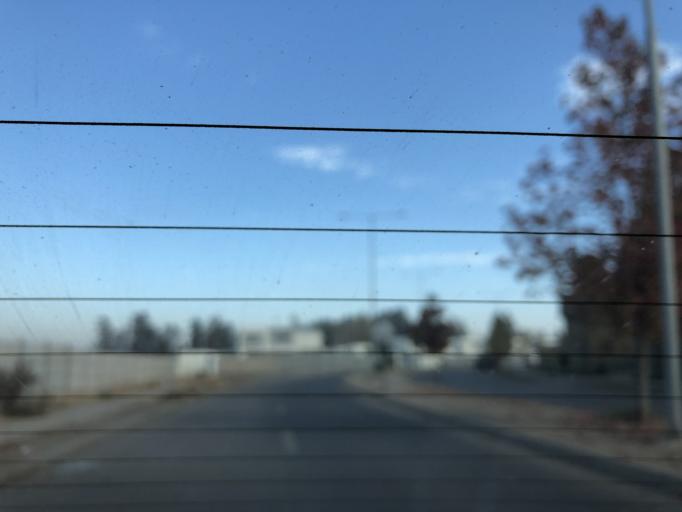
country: CL
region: Santiago Metropolitan
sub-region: Provincia de Cordillera
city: Puente Alto
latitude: -33.6002
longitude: -70.5185
